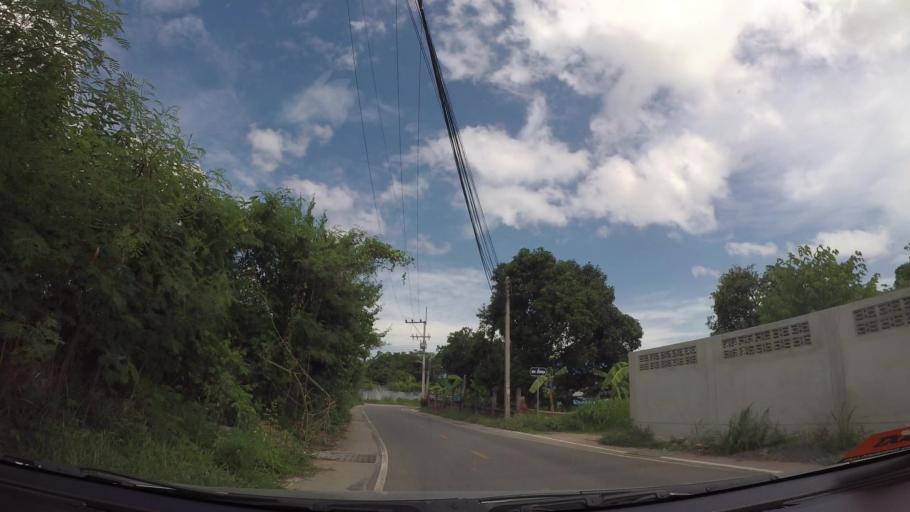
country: TH
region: Chon Buri
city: Sattahip
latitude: 12.6891
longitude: 100.9015
